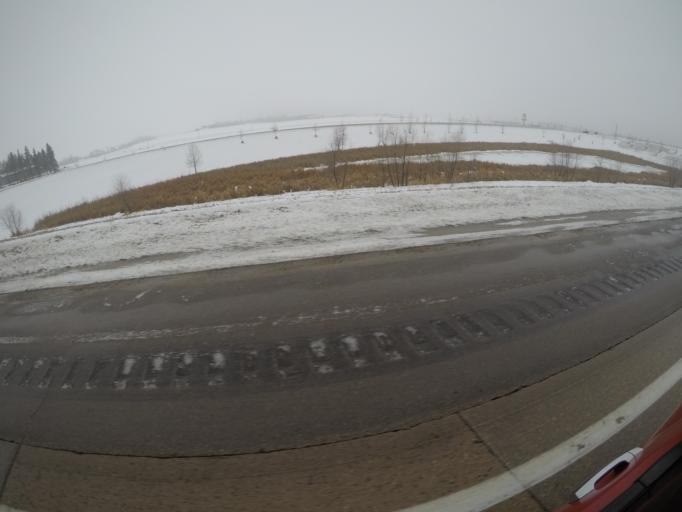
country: US
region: Minnesota
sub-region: Olmsted County
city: Oronoco
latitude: 44.1430
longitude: -92.5278
